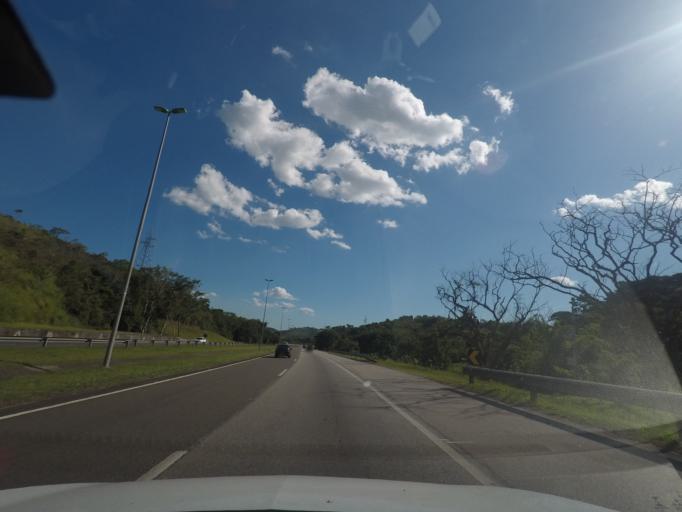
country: BR
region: Rio de Janeiro
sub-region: Guapimirim
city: Guapimirim
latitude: -22.5967
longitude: -43.0243
